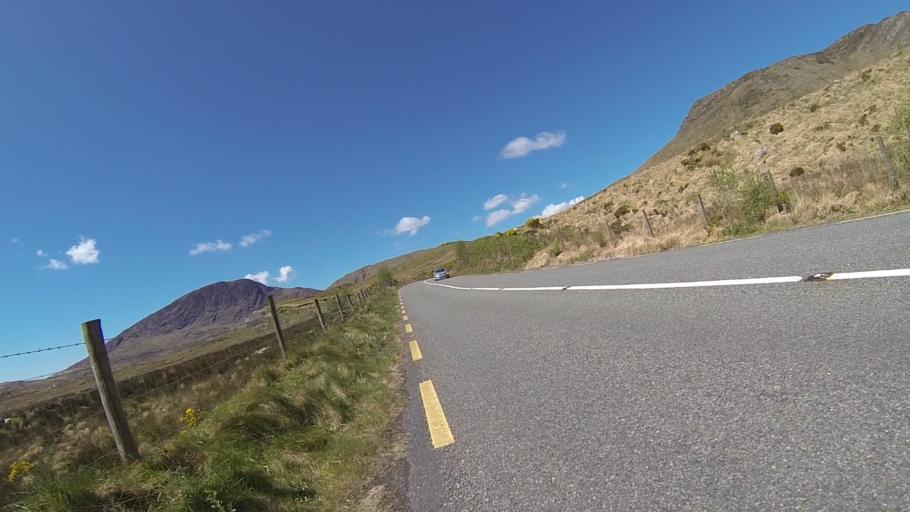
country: IE
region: Munster
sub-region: Ciarrai
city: Kenmare
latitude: 51.9269
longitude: -9.6406
